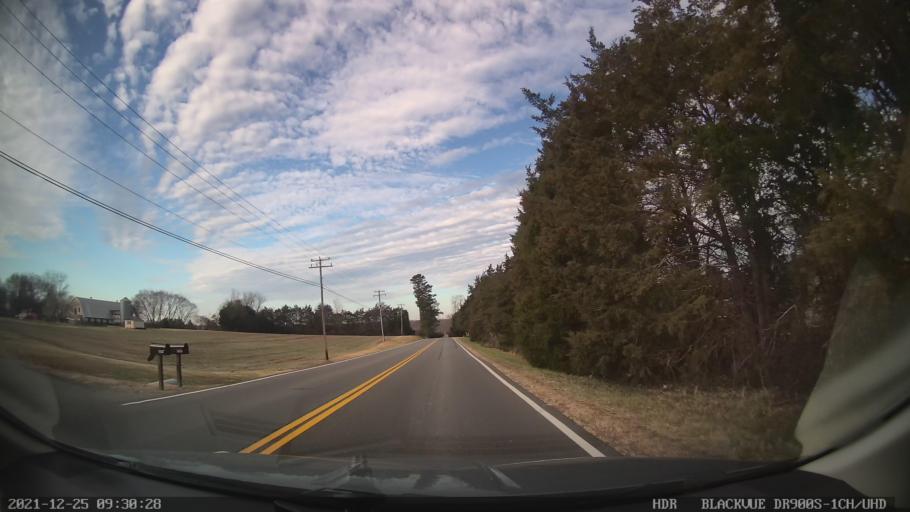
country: US
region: Virginia
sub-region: Goochland County
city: Goochland
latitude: 37.7102
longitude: -77.8048
